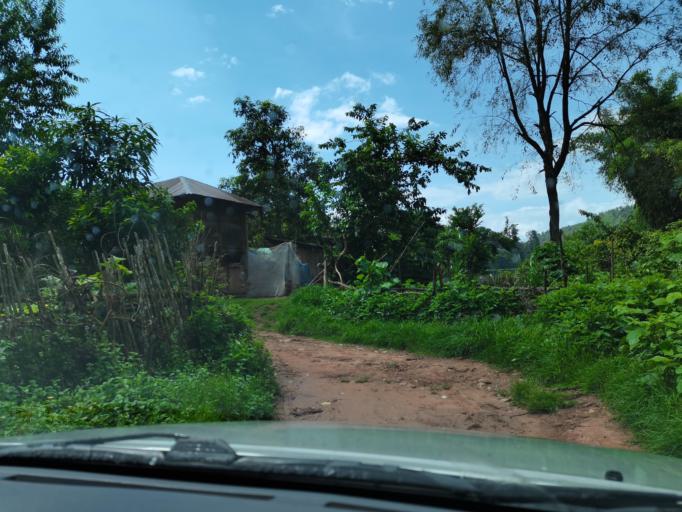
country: LA
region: Loungnamtha
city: Muang Nale
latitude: 20.5270
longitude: 101.0658
